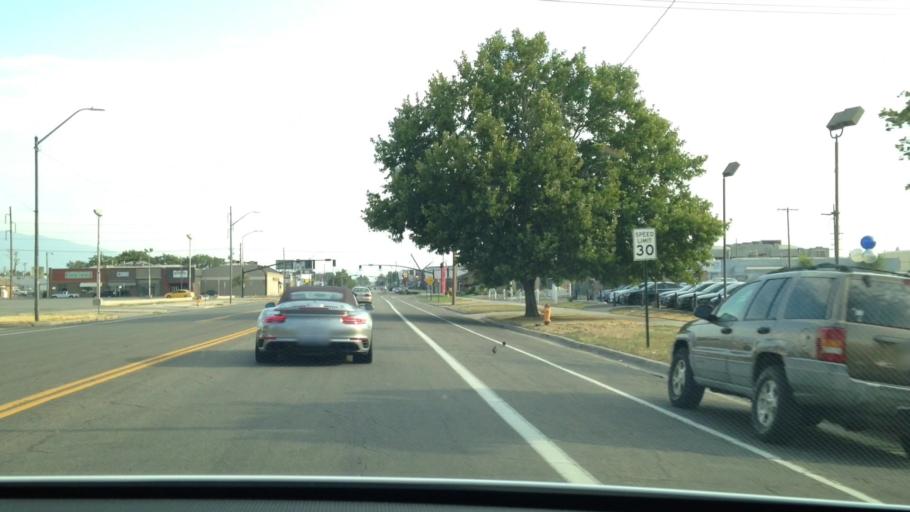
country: US
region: Utah
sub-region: Salt Lake County
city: Salt Lake City
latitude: 40.7538
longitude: -111.8910
